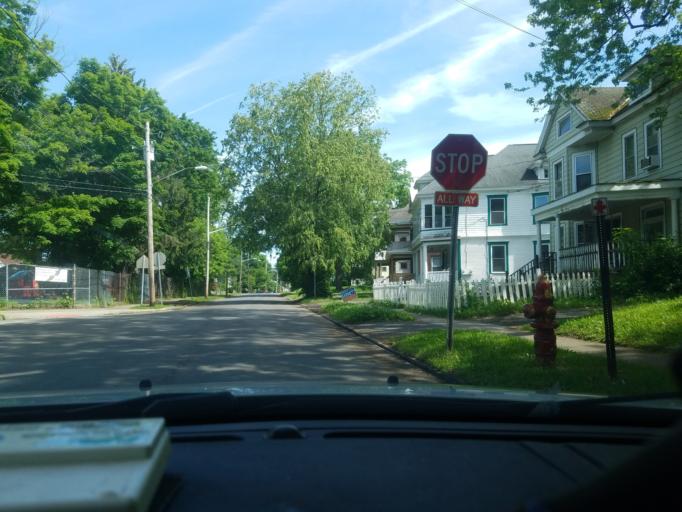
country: US
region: New York
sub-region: Onondaga County
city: Syracuse
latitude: 43.0426
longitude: -76.1222
